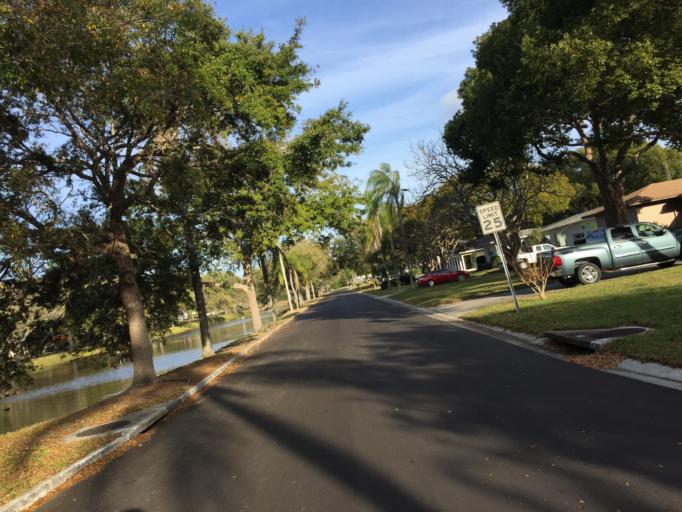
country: US
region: Florida
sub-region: Pinellas County
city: Clearwater
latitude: 27.9763
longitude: -82.7792
